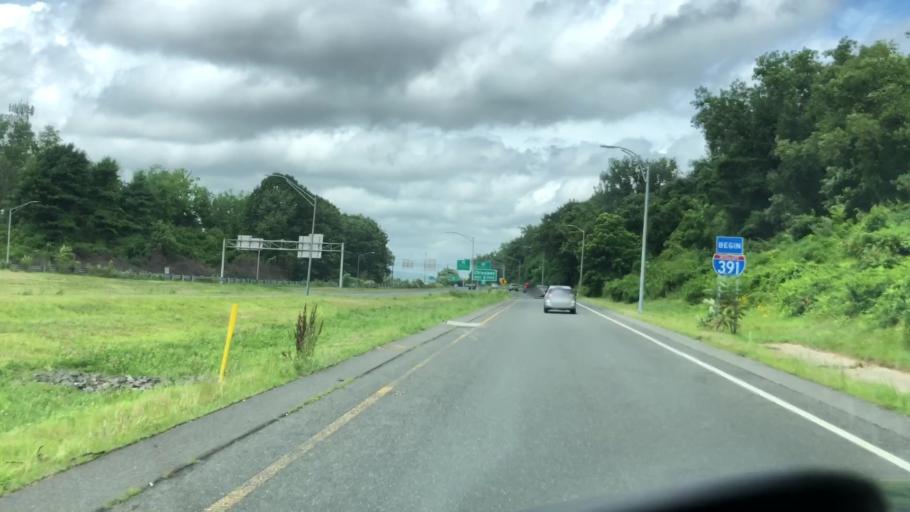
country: US
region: Massachusetts
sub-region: Hampden County
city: Chicopee
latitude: 42.1353
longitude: -72.6084
